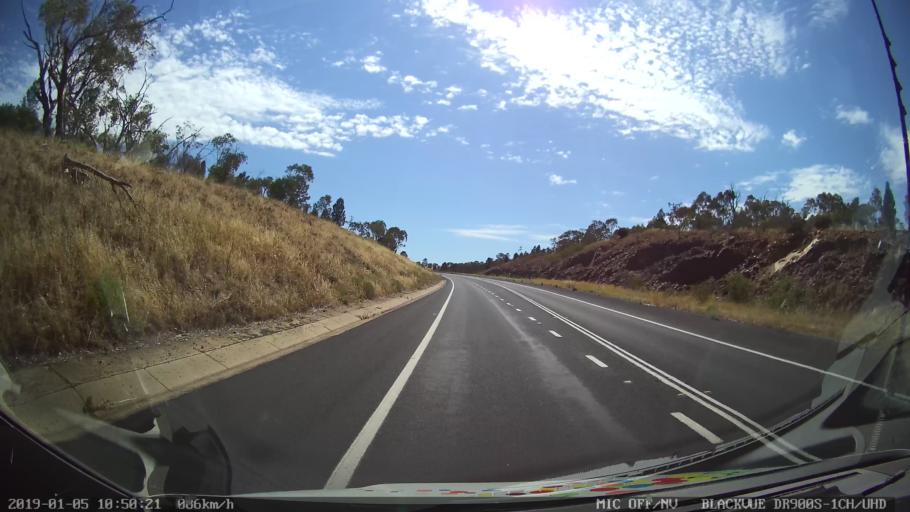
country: AU
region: New South Wales
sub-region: Warrumbungle Shire
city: Coonabarabran
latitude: -31.4293
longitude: 149.0743
